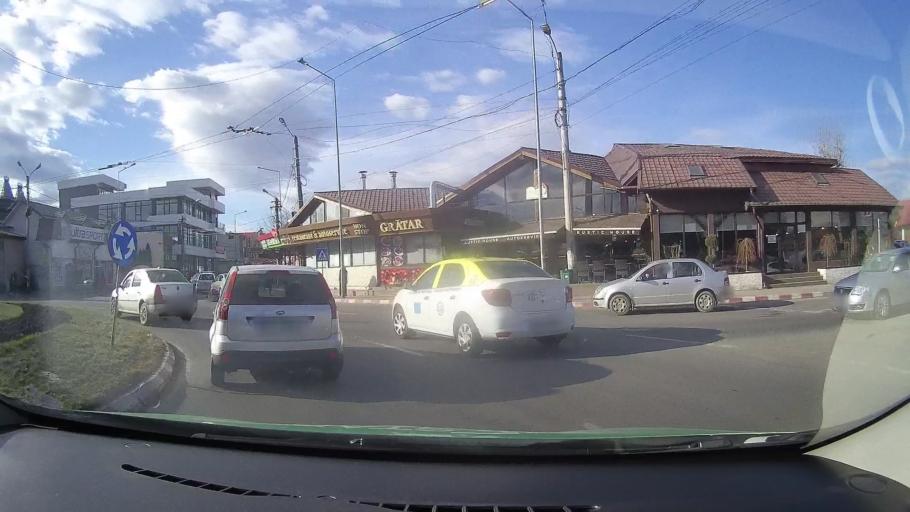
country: RO
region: Dambovita
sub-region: Comuna Lucieni
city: Lucieni
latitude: 44.8589
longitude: 25.4186
